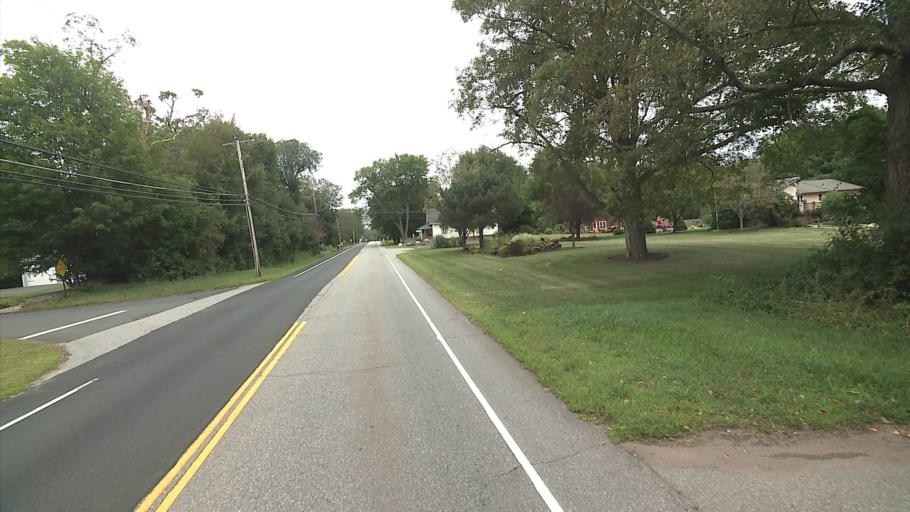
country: US
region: Connecticut
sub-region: Hartford County
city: Manchester
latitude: 41.7456
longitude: -72.4375
